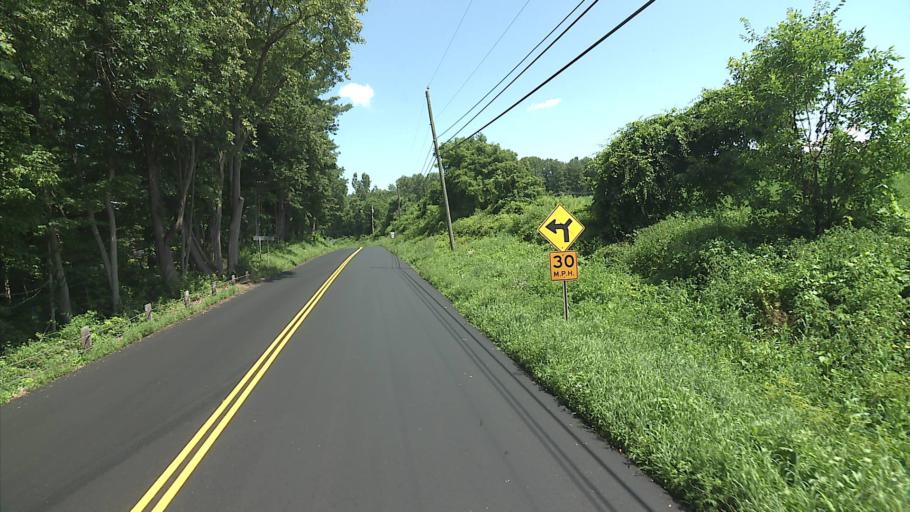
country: US
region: Connecticut
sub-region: Litchfield County
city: Canaan
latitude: 42.0031
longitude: -73.3565
